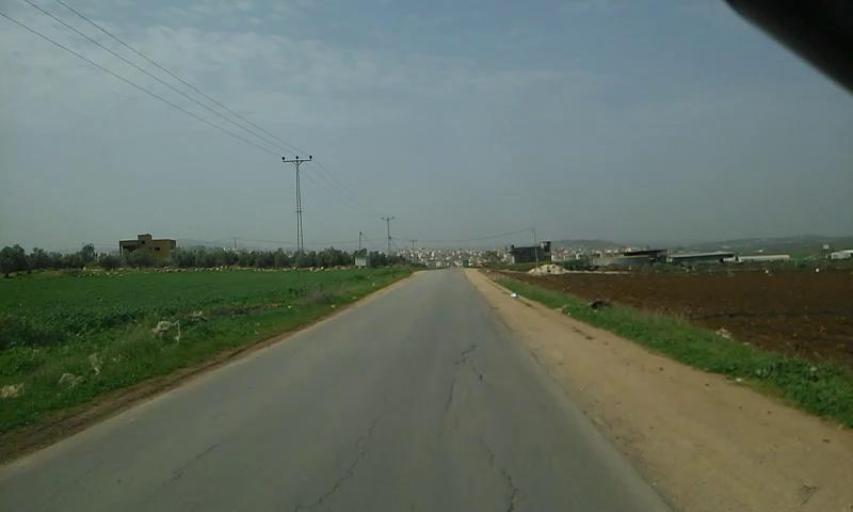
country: PS
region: West Bank
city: Silat al Harithiyah
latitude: 32.5008
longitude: 35.2463
